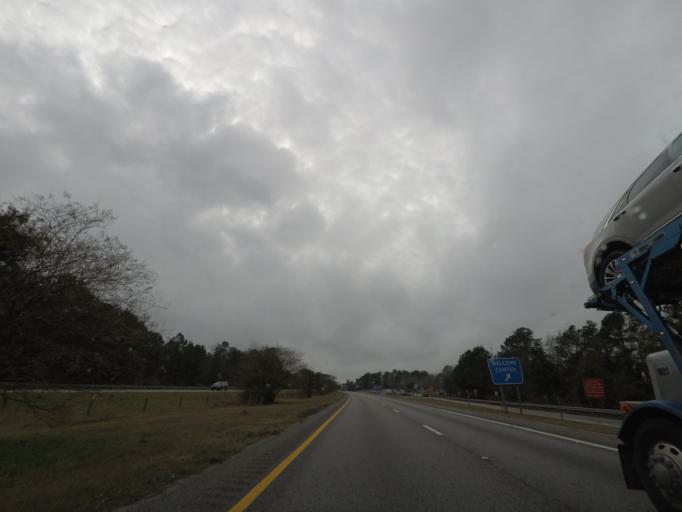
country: US
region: South Carolina
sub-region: Orangeburg County
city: Holly Hill
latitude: 33.4951
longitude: -80.4657
